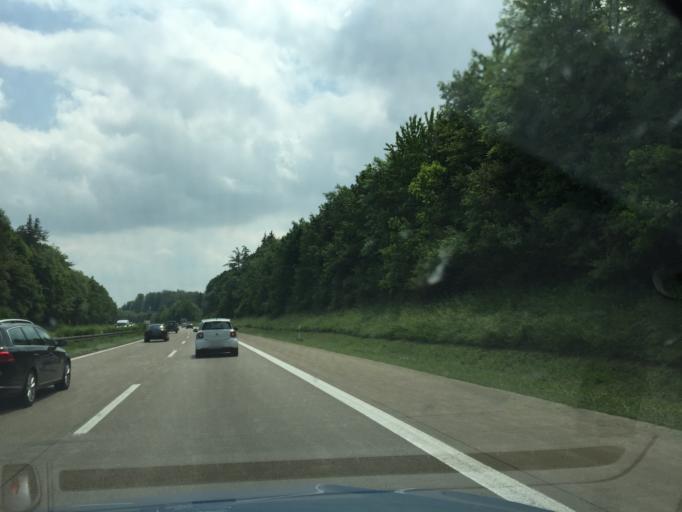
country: DE
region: Baden-Wuerttemberg
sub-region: Regierungsbezirk Stuttgart
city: Westhausen
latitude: 48.8488
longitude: 10.1972
